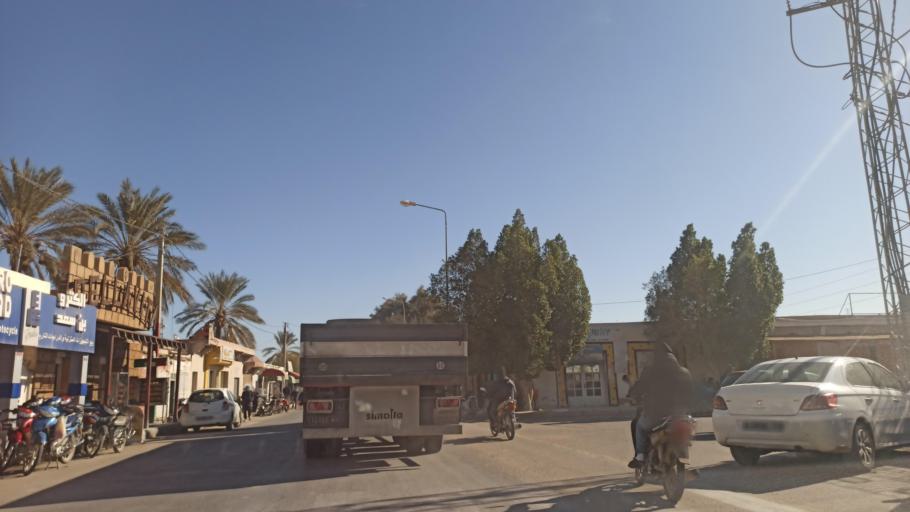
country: TN
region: Gafsa
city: Al Metlaoui
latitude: 34.3156
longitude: 8.4027
